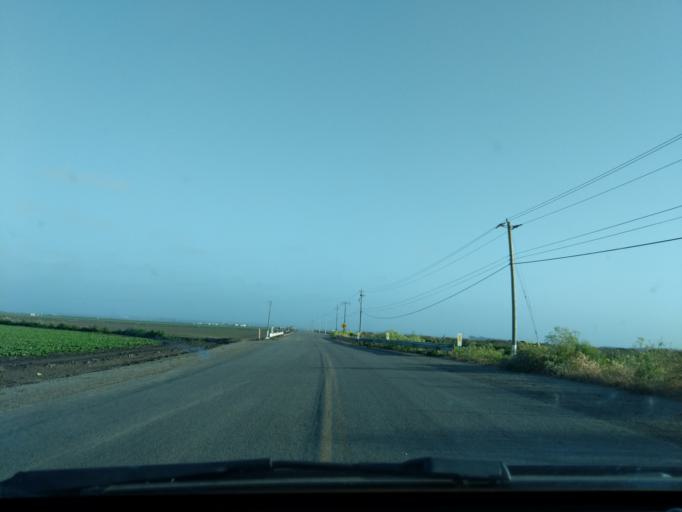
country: US
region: California
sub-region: Monterey County
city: Castroville
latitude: 36.7730
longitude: -121.7877
